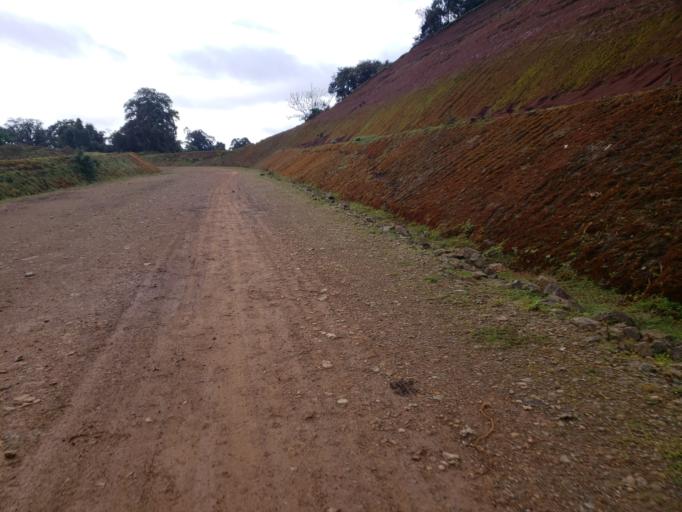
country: ET
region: Oromiya
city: Dodola
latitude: 6.6706
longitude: 39.3641
